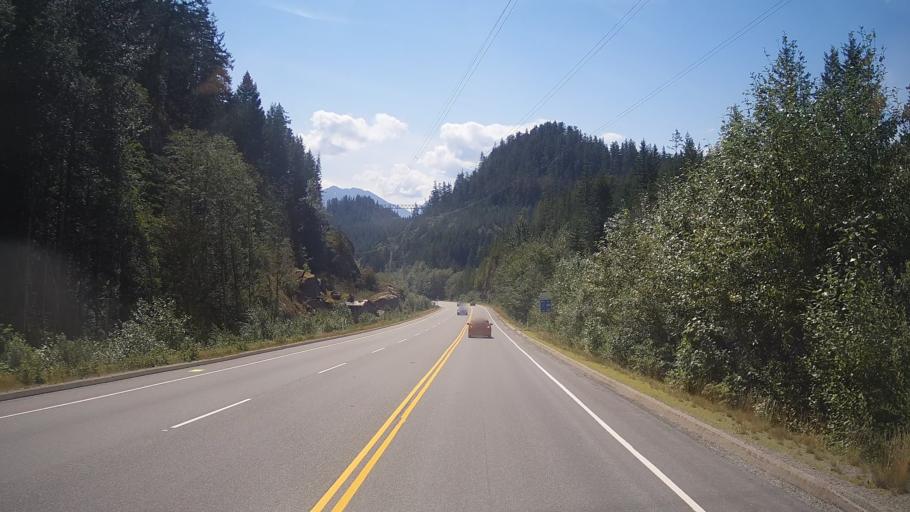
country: CA
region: British Columbia
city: Whistler
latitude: 49.8267
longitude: -123.1347
